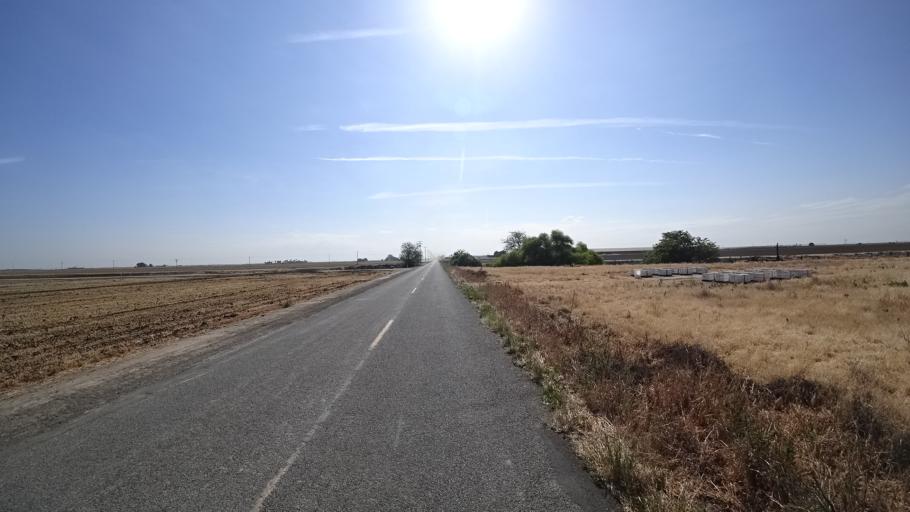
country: US
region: California
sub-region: Kings County
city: Home Garden
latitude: 36.2260
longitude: -119.5612
